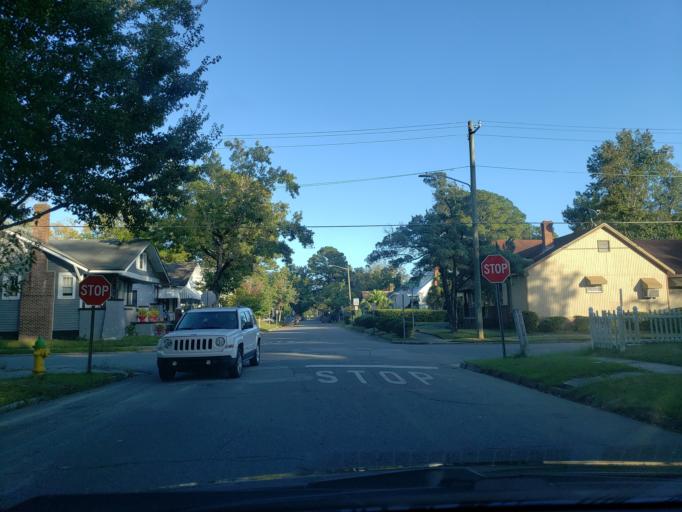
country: US
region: Georgia
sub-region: Chatham County
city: Savannah
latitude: 32.0549
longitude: -81.0871
